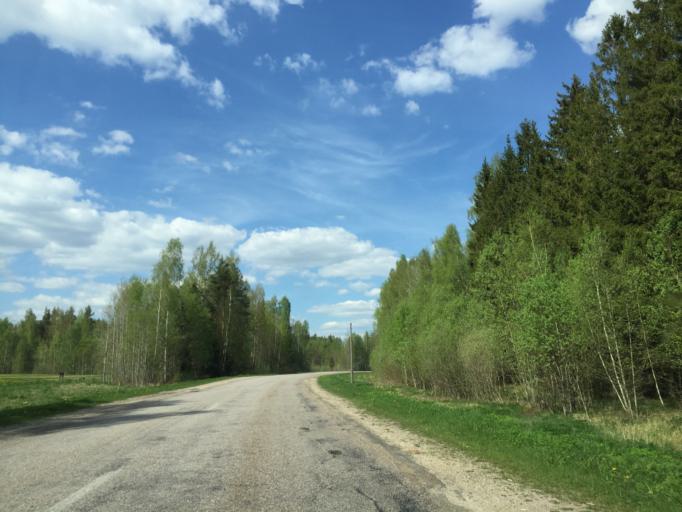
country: LV
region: Limbazu Rajons
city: Limbazi
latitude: 57.4046
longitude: 24.6908
